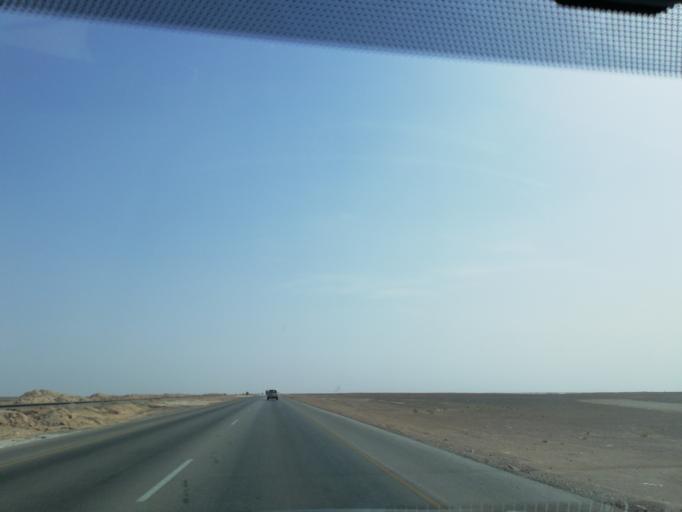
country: OM
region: Muhafazat ad Dakhiliyah
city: Adam
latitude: 21.6228
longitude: 57.3001
